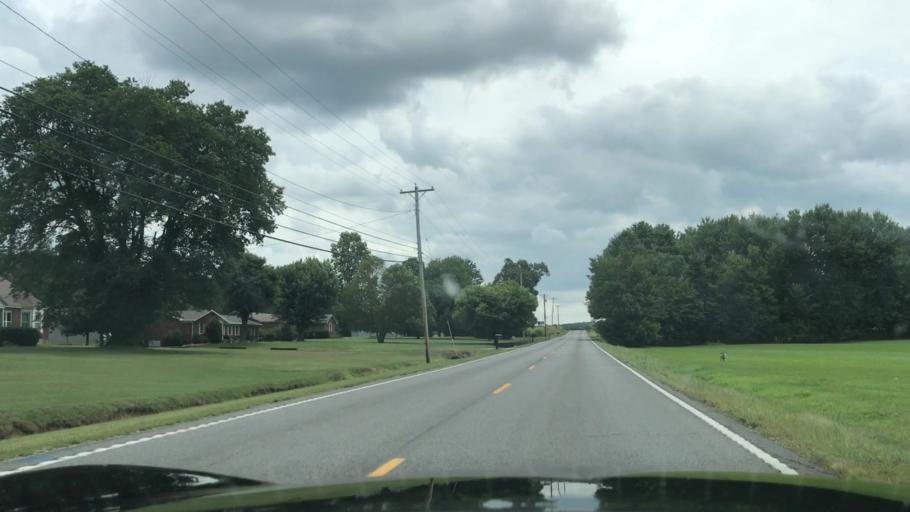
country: US
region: Kentucky
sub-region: Muhlenberg County
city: Greenville
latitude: 37.2006
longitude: -87.1361
